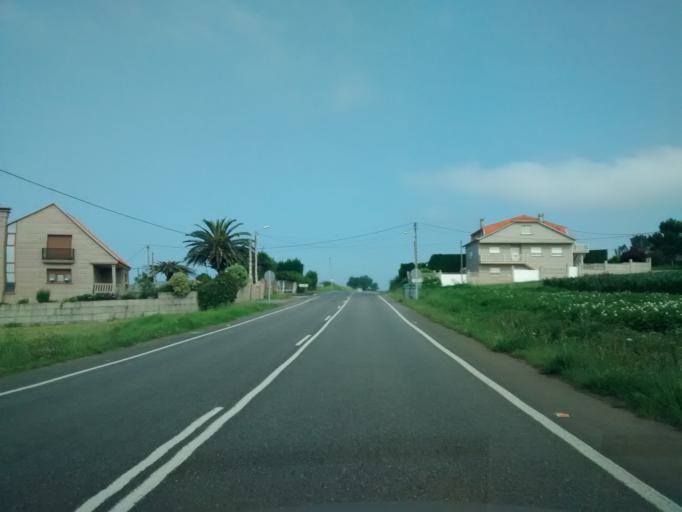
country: ES
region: Galicia
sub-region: Provincia de Pontevedra
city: Sanxenxo
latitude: 42.4105
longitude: -8.8597
